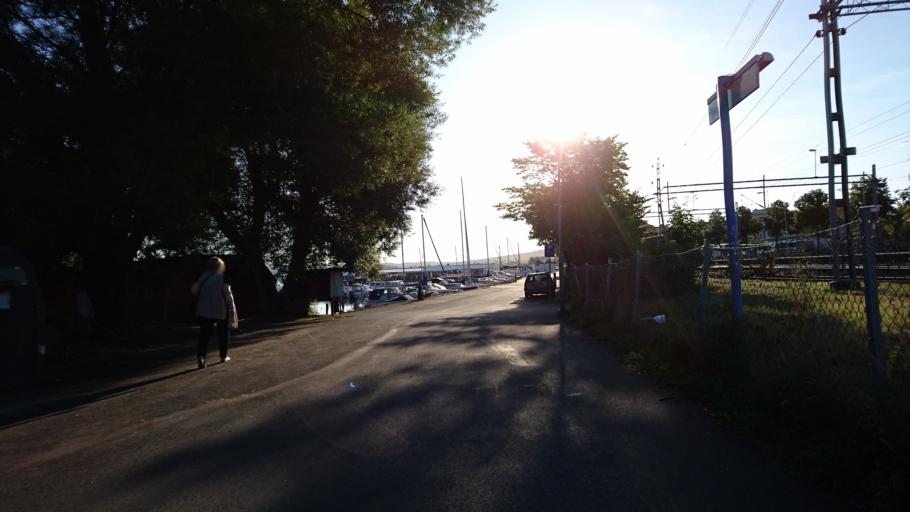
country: SE
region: Joenkoeping
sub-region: Jonkopings Kommun
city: Jonkoping
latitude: 57.7845
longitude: 14.1657
